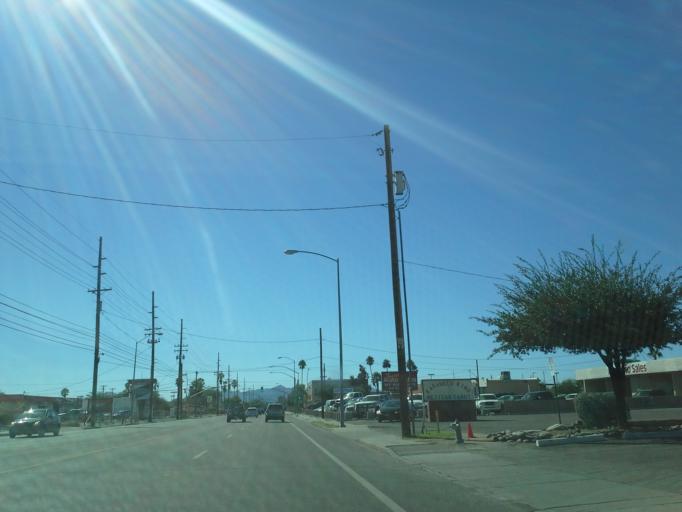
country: US
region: Arizona
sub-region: Pima County
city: Tucson
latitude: 32.2507
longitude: -110.9121
